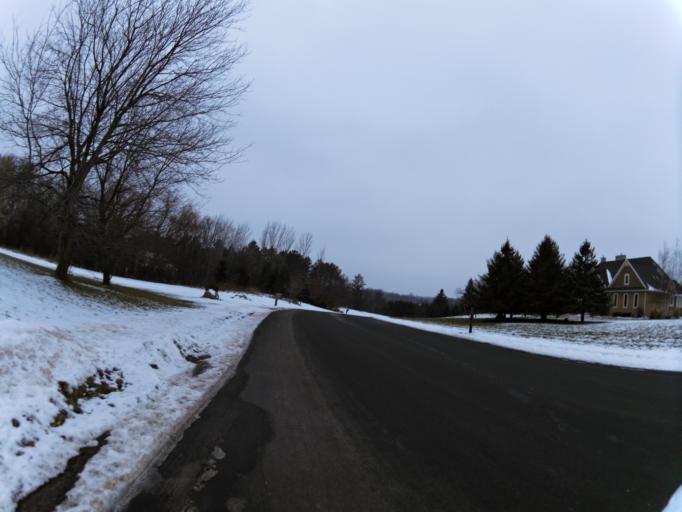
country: US
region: Minnesota
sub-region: Washington County
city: Lake Elmo
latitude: 44.9677
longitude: -92.8463
